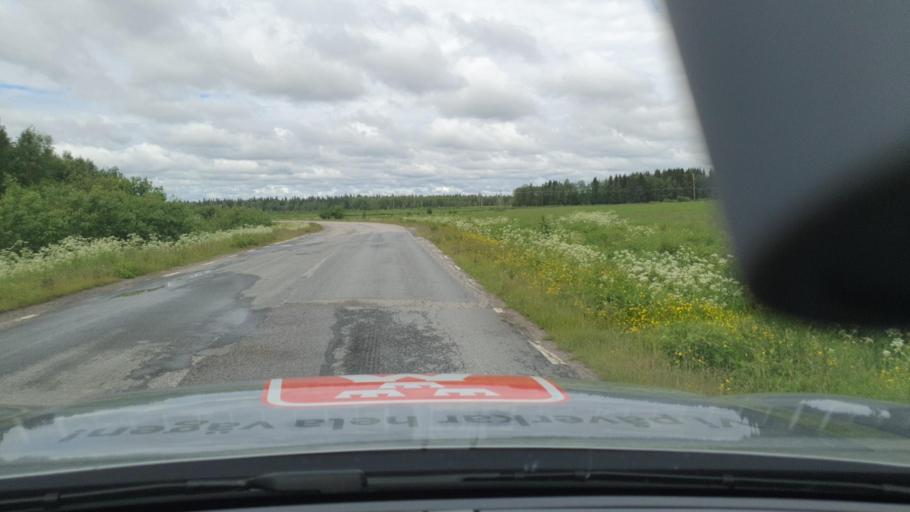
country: SE
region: Norrbotten
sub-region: Lulea Kommun
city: Ranea
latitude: 65.7764
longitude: 22.2273
